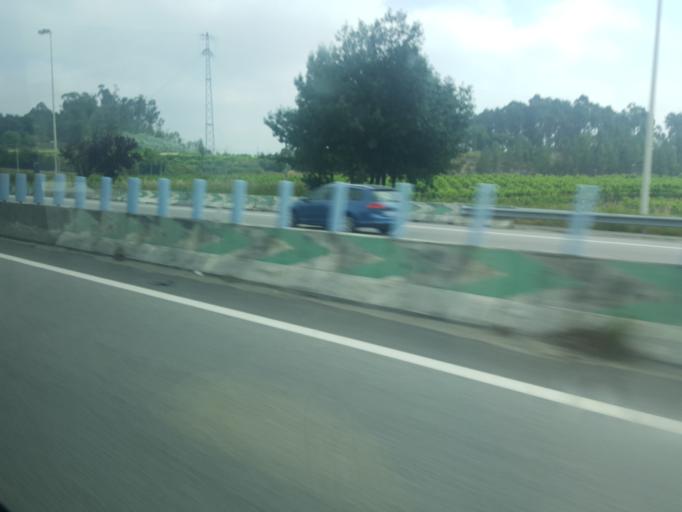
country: PT
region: Porto
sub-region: Lousada
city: Meinedo
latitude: 41.2356
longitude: -8.2064
